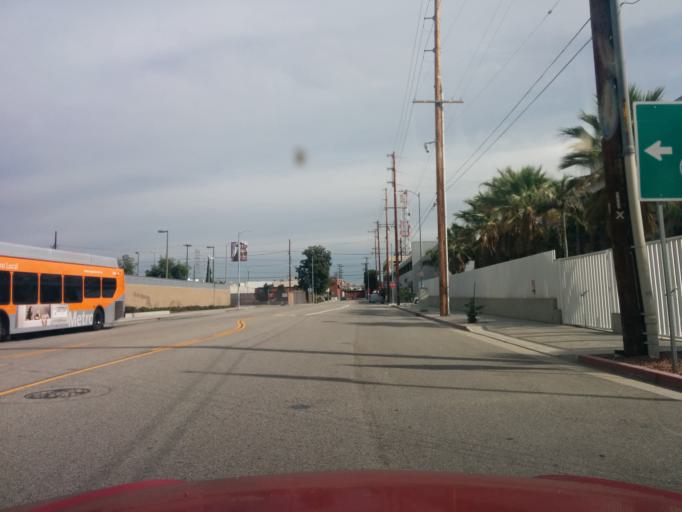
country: US
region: California
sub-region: Los Angeles County
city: Los Angeles
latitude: 34.0504
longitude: -118.2354
